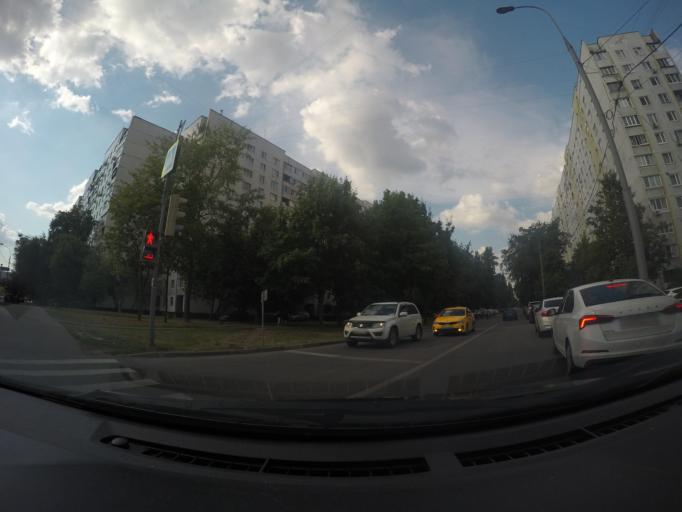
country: RU
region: Moscow
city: Kozeyevo
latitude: 55.8577
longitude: 37.6089
